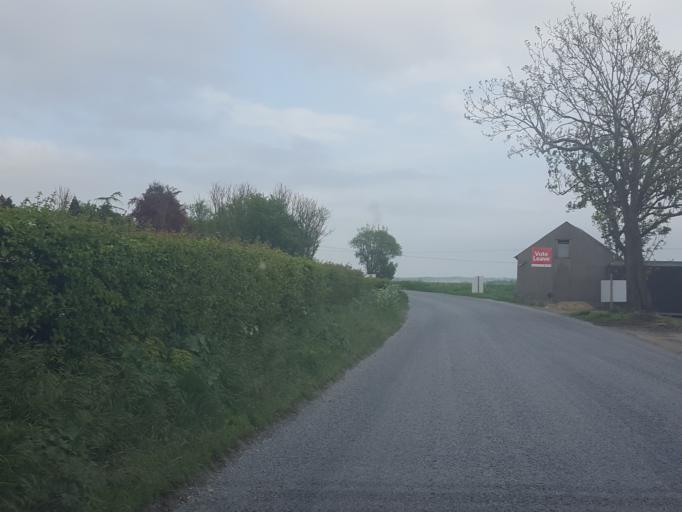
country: GB
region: England
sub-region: Essex
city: Frinton-on-Sea
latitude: 51.8528
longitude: 1.2002
